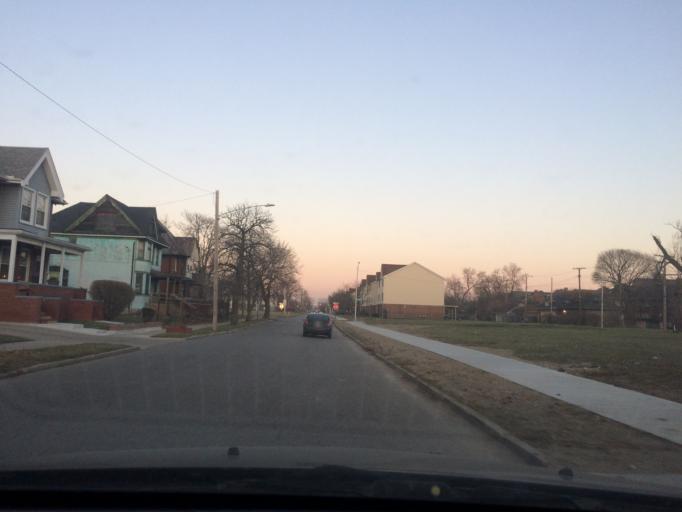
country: US
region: Michigan
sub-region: Wayne County
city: Highland Park
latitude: 42.3756
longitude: -83.0821
